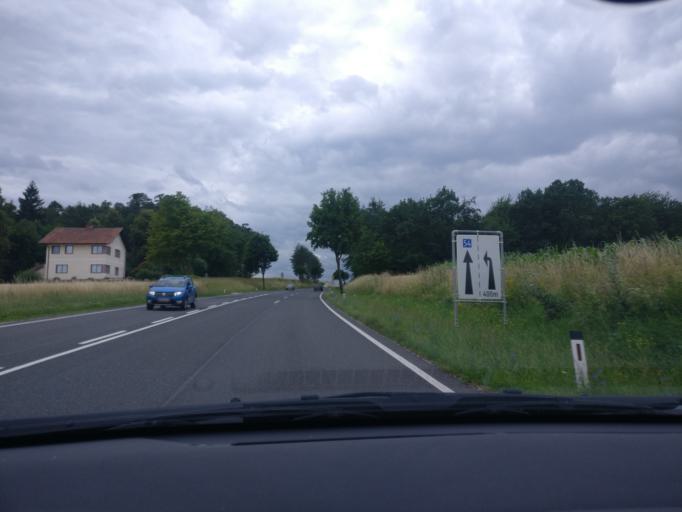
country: AT
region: Lower Austria
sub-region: Politischer Bezirk Neunkirchen
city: Breitenau
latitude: 47.7145
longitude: 16.1481
